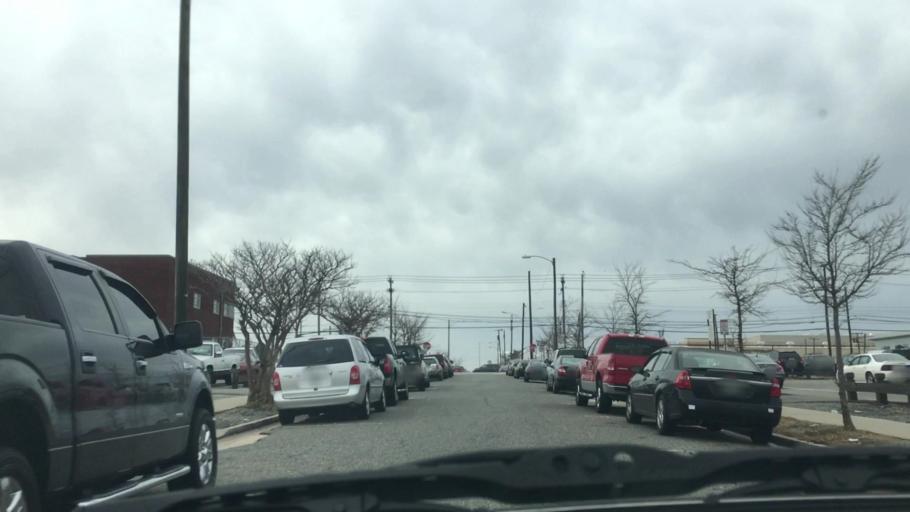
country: US
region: Virginia
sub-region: City of Newport News
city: Newport News
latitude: 36.9910
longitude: -76.4351
